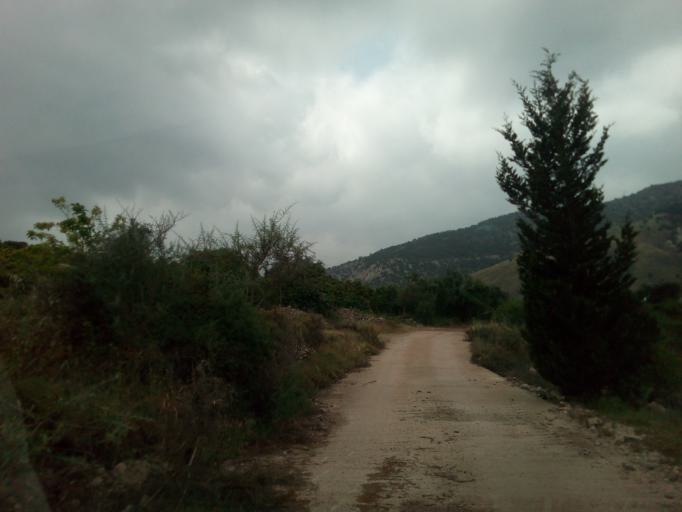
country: CY
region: Limassol
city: Pissouri
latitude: 34.8146
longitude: 32.6266
